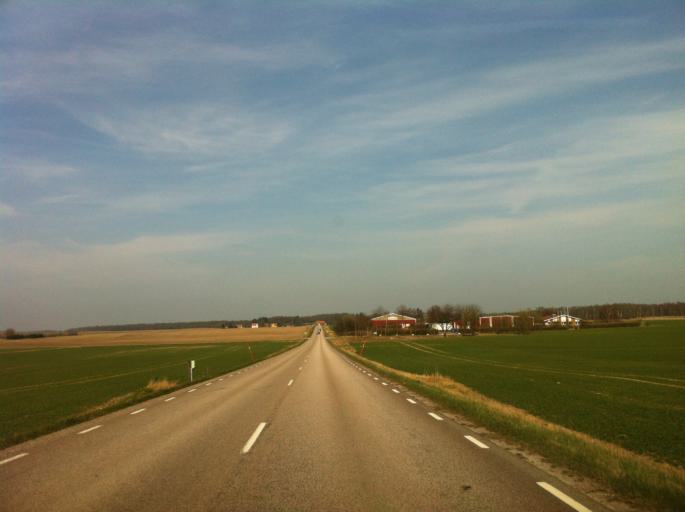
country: SE
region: Skane
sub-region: Svalovs Kommun
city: Svaloev
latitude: 55.9309
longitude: 13.1082
